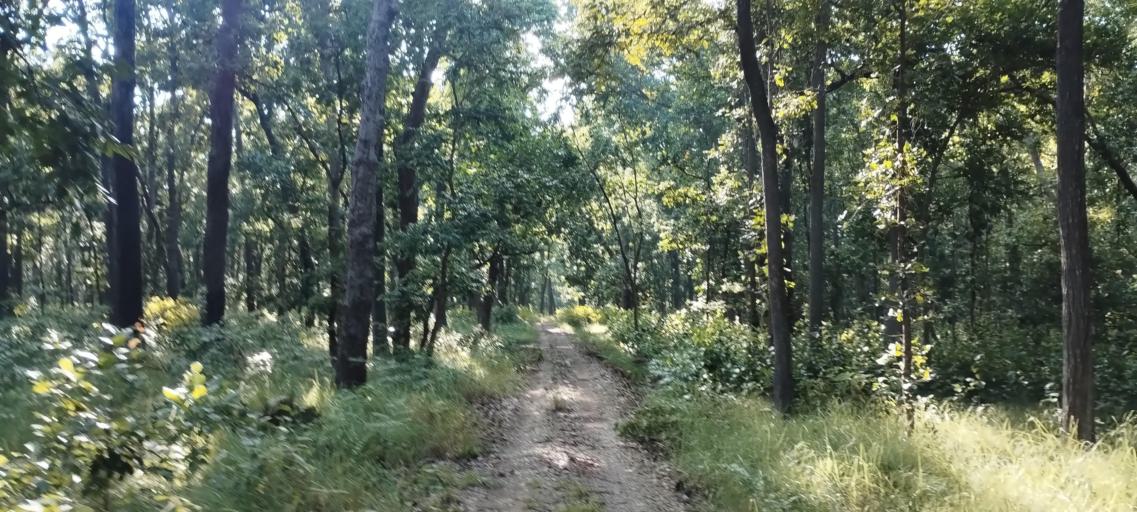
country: NP
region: Far Western
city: Tikapur
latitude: 28.5226
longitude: 81.2656
